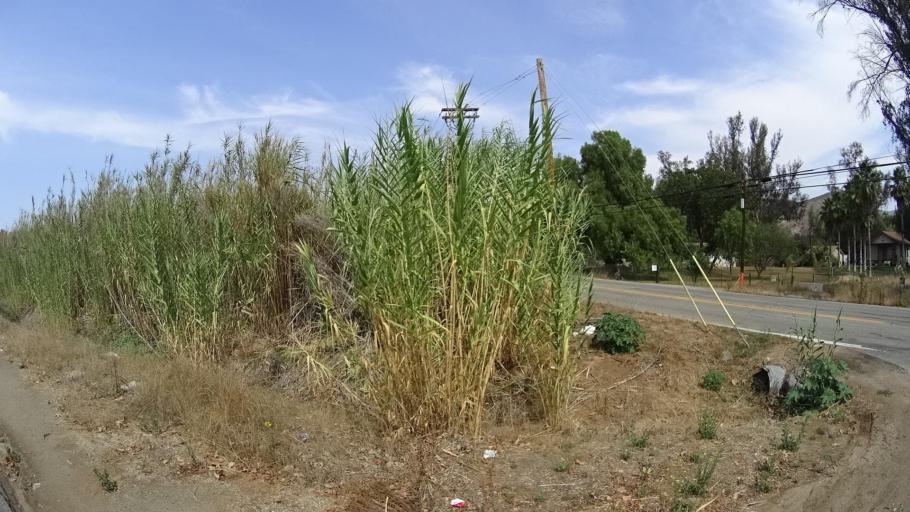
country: US
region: California
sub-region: San Diego County
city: San Pasqual
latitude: 33.0939
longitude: -117.0209
